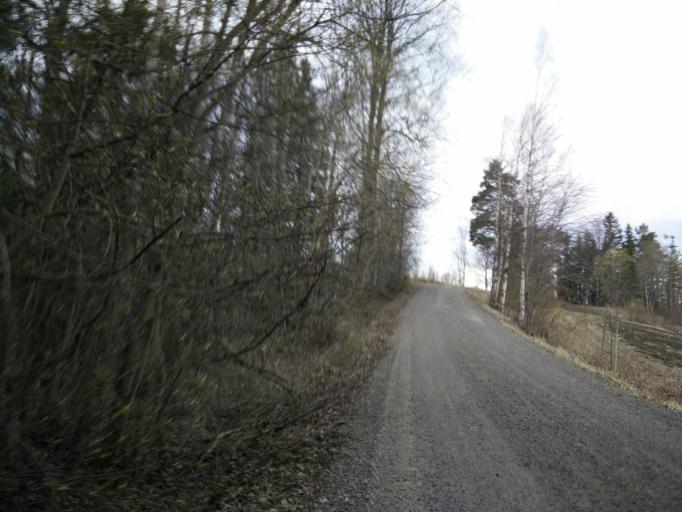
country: FI
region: Pirkanmaa
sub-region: Tampere
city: Orivesi
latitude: 61.7048
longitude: 24.3136
